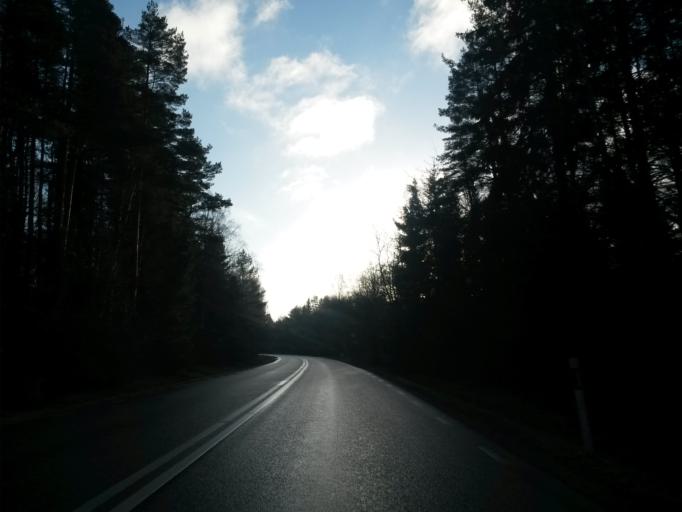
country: SE
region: Vaestra Goetaland
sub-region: Vargarda Kommun
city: Vargarda
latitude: 57.9697
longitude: 12.8113
